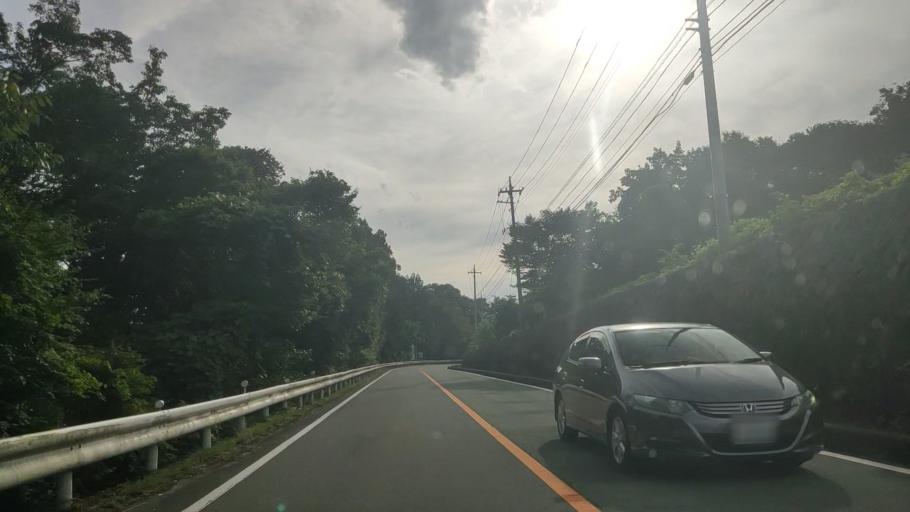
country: JP
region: Gunma
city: Omamacho-omama
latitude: 36.5314
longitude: 139.3307
